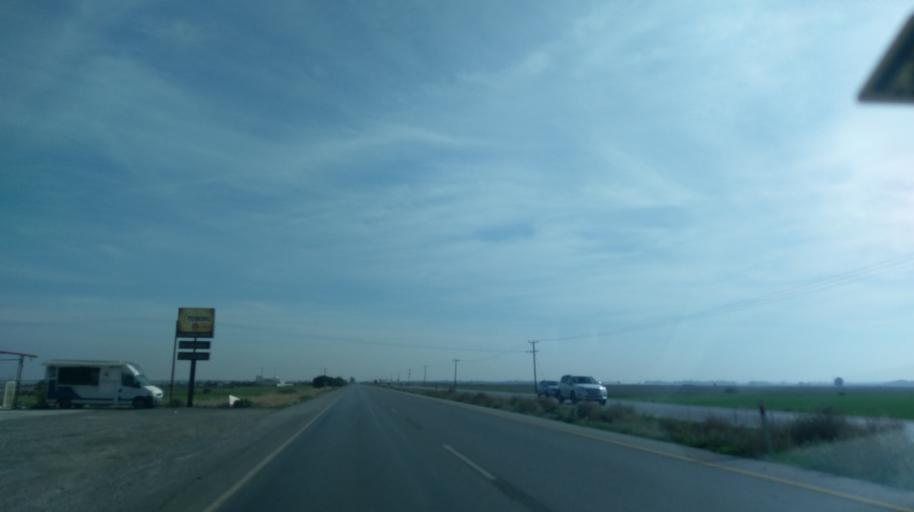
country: CY
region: Larnaka
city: Athienou
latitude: 35.2116
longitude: 33.5335
